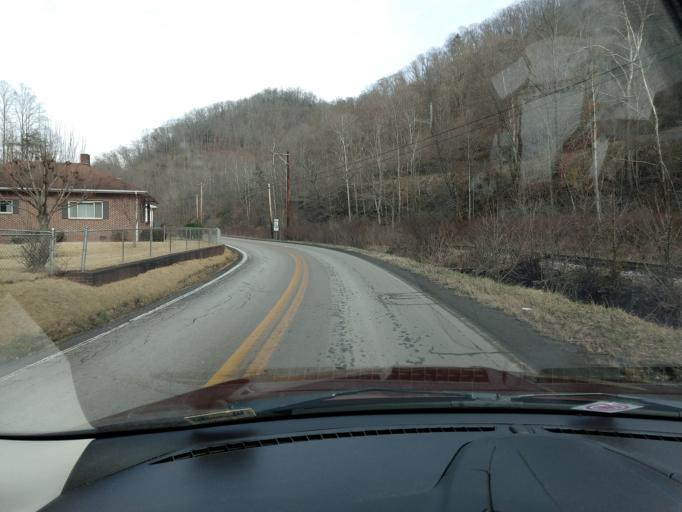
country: US
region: West Virginia
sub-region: McDowell County
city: Welch
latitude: 37.3234
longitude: -81.6891
